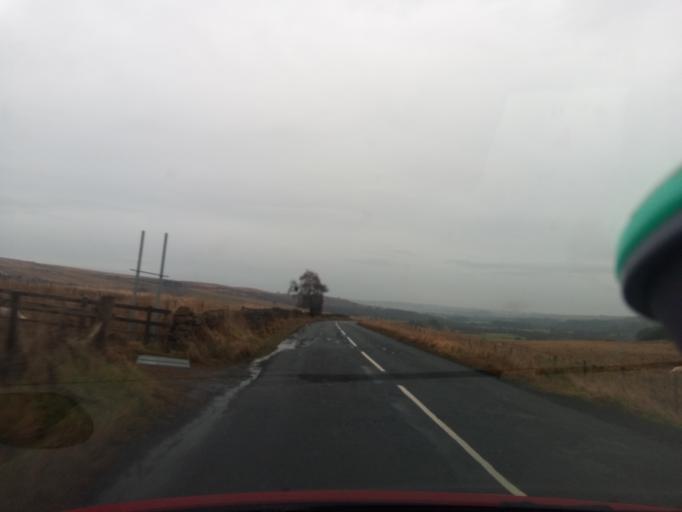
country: GB
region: England
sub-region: Northumberland
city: Rochester
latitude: 55.1643
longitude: -2.3208
